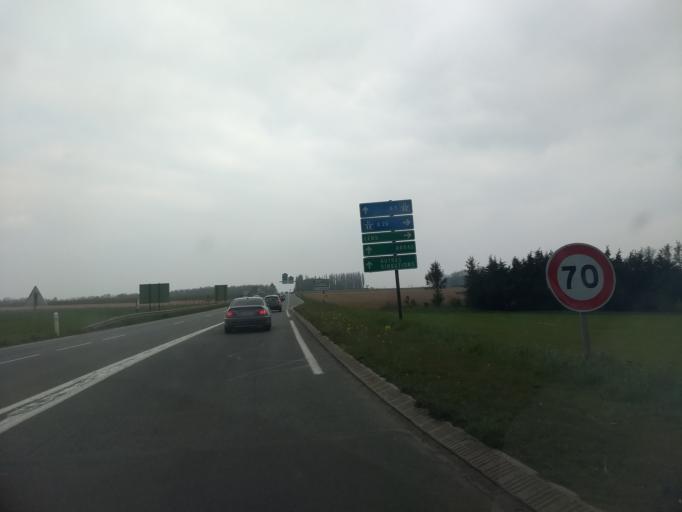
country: FR
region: Nord-Pas-de-Calais
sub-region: Departement du Pas-de-Calais
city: Sainte-Catherine
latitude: 50.3236
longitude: 2.7605
